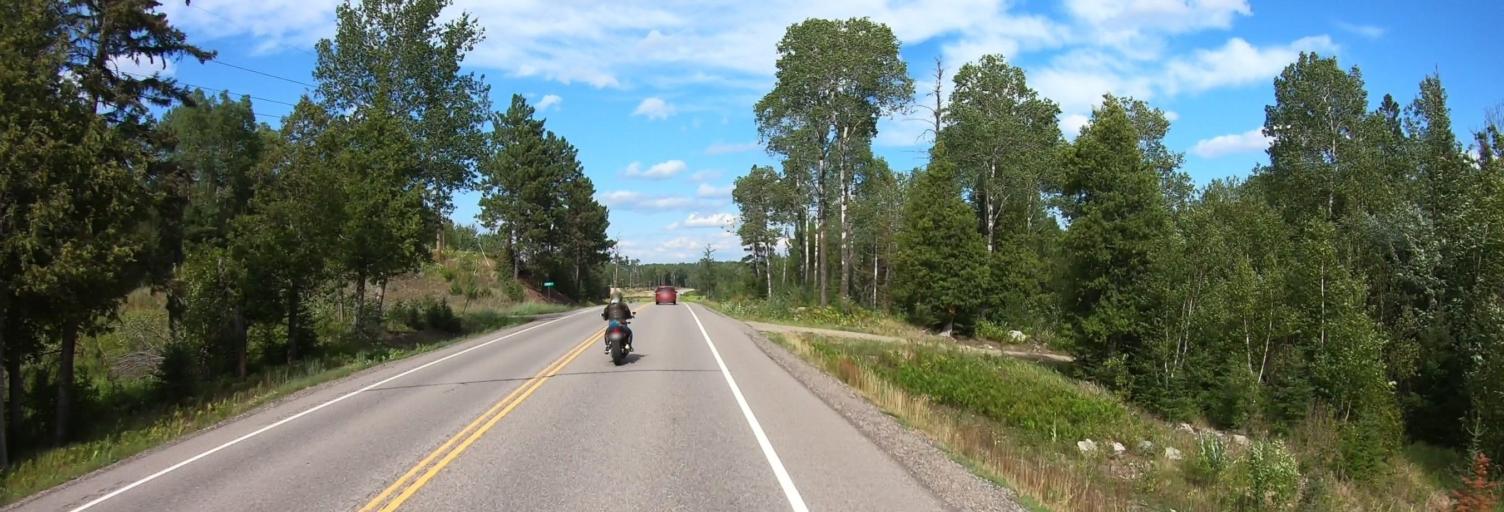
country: US
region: Minnesota
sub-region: Saint Louis County
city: Ely
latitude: 47.8771
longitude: -92.0146
